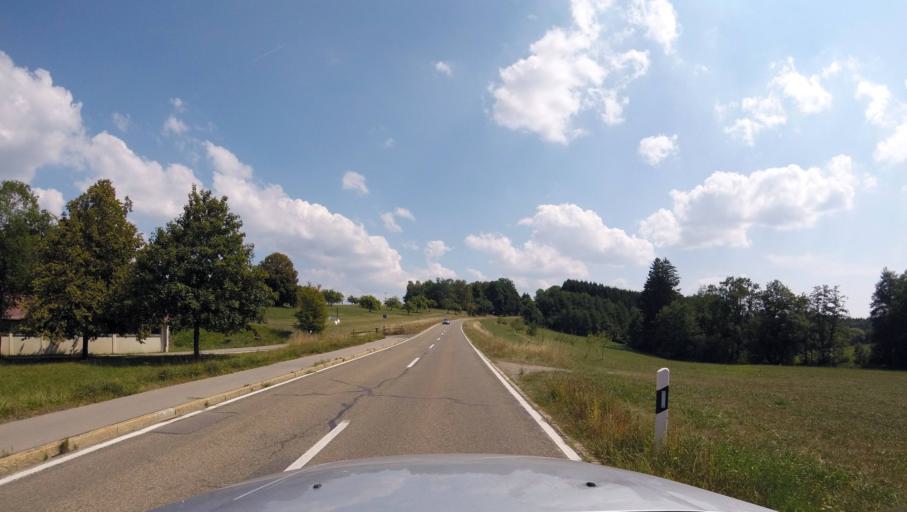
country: DE
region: Baden-Wuerttemberg
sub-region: Regierungsbezirk Stuttgart
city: Welzheim
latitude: 48.8738
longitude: 9.6431
